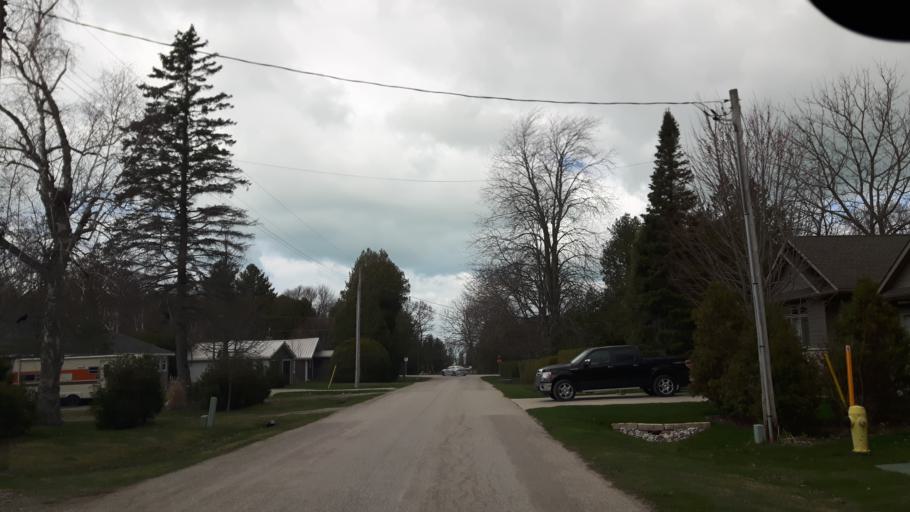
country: CA
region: Ontario
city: Bluewater
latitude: 43.5617
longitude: -81.7033
